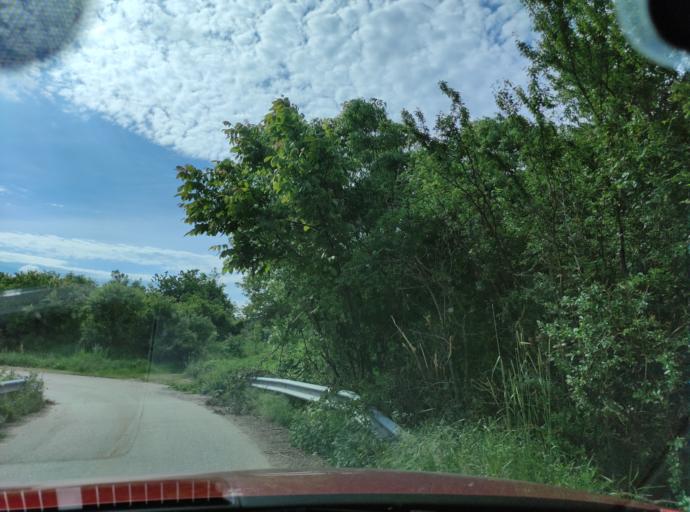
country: BG
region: Vidin
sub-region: Obshtina Belogradchik
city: Belogradchik
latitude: 43.5174
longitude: 22.7281
